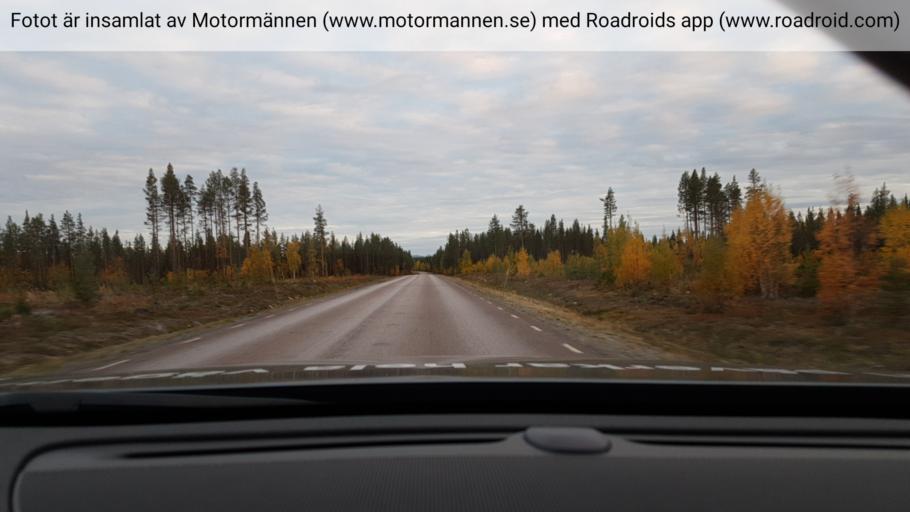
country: SE
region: Norrbotten
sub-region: Jokkmokks Kommun
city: Jokkmokk
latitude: 66.0362
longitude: 20.1226
